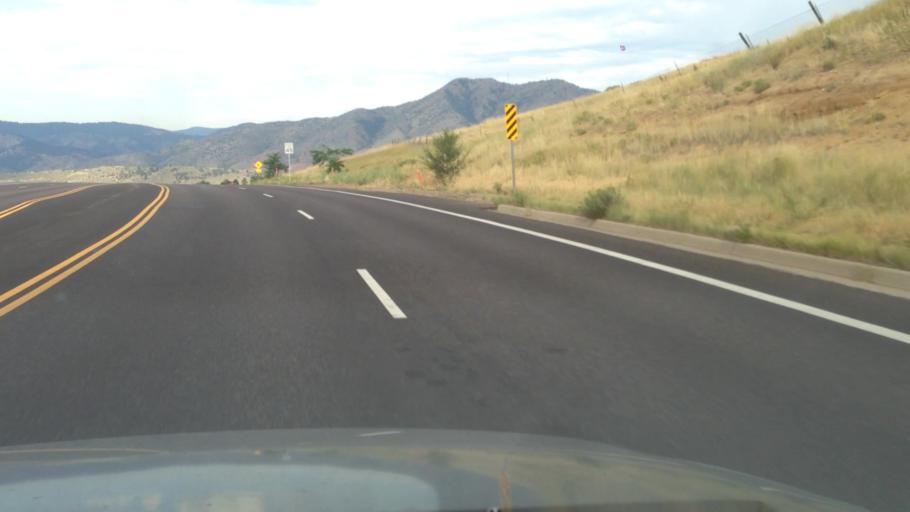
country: US
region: Colorado
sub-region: Jefferson County
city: West Pleasant View
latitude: 39.6812
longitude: -105.1629
